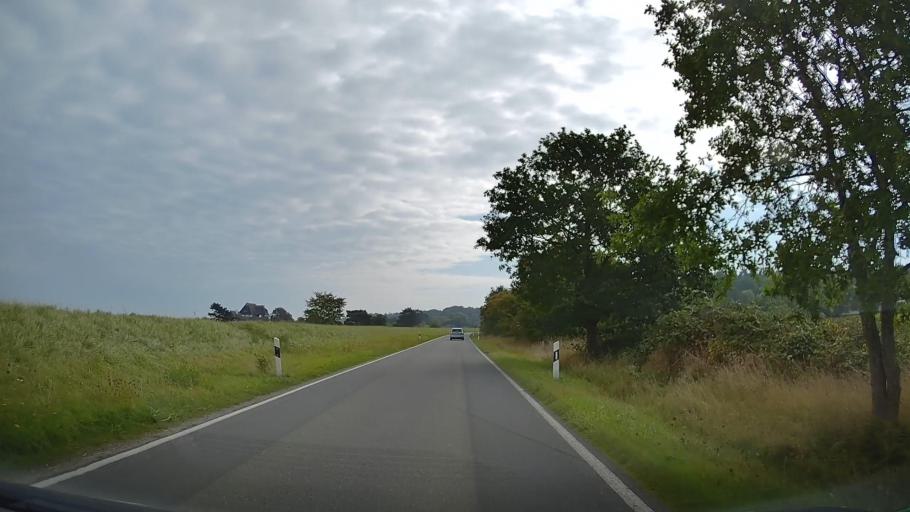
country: DE
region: Schleswig-Holstein
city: Blekendorf
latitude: 54.3285
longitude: 10.6540
